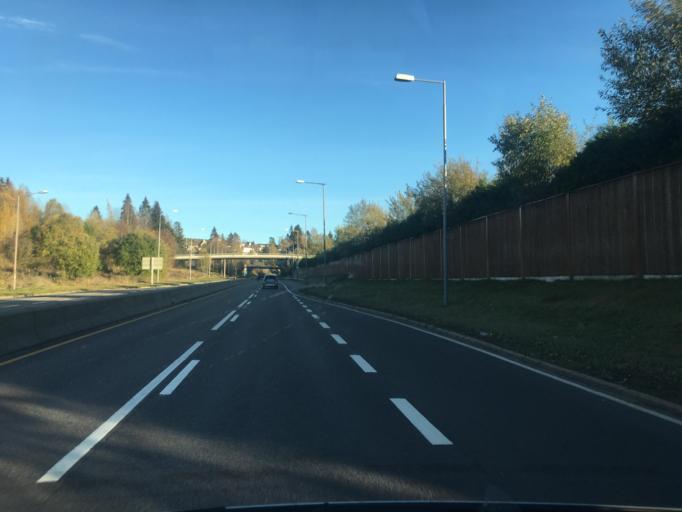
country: NO
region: Akershus
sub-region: Lorenskog
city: Kjenn
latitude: 59.9523
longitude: 10.9223
